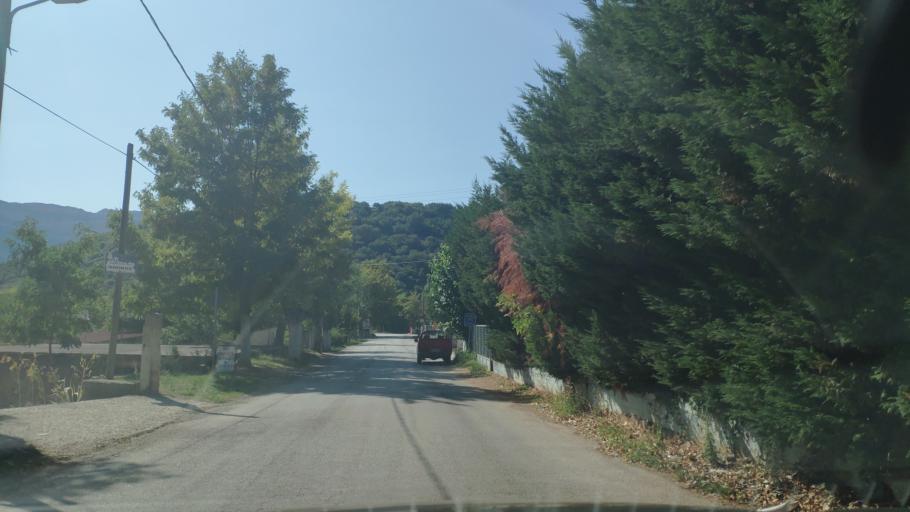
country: GR
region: Peloponnese
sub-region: Nomos Korinthias
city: Nemea
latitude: 37.8891
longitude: 22.4975
